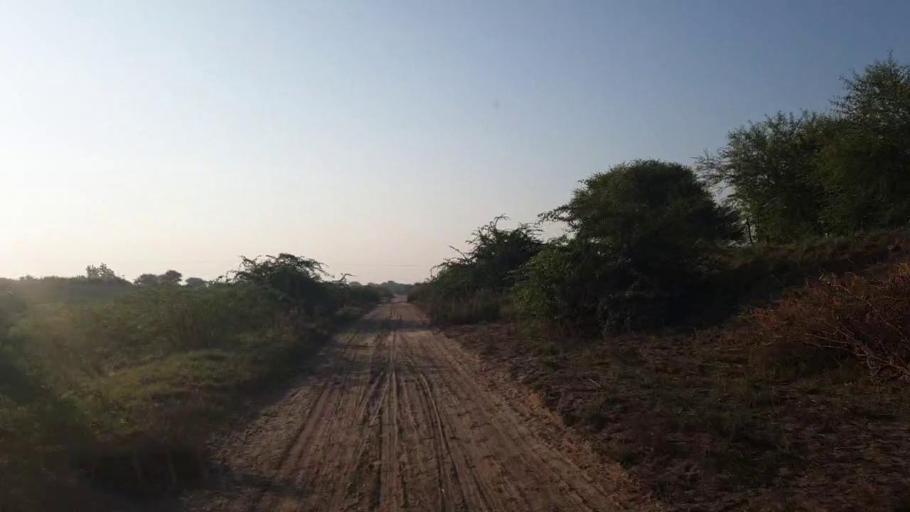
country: PK
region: Sindh
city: Badin
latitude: 24.6329
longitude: 68.7950
